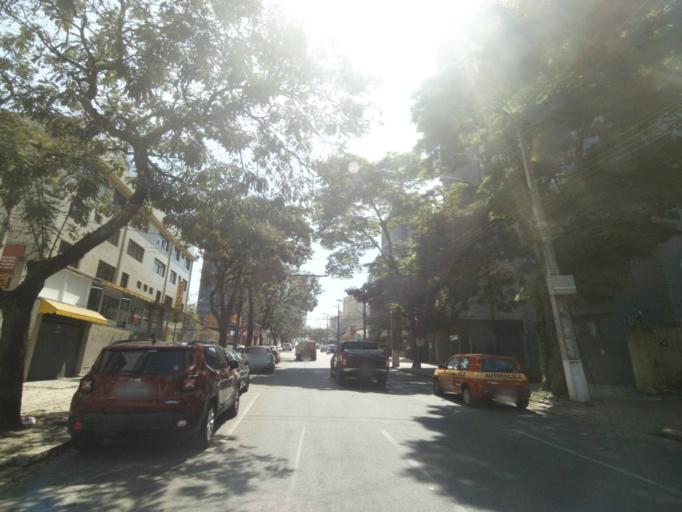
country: BR
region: Parana
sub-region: Curitiba
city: Curitiba
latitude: -25.4699
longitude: -49.2913
